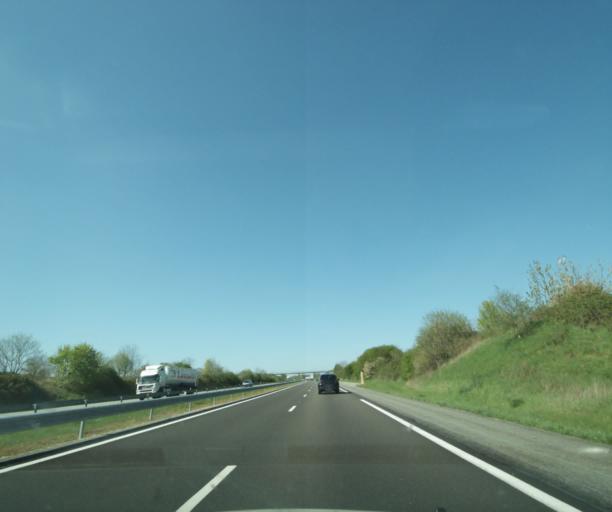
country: FR
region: Bourgogne
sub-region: Departement de la Nievre
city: Cosne-Cours-sur-Loire
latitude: 47.4804
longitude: 2.9437
